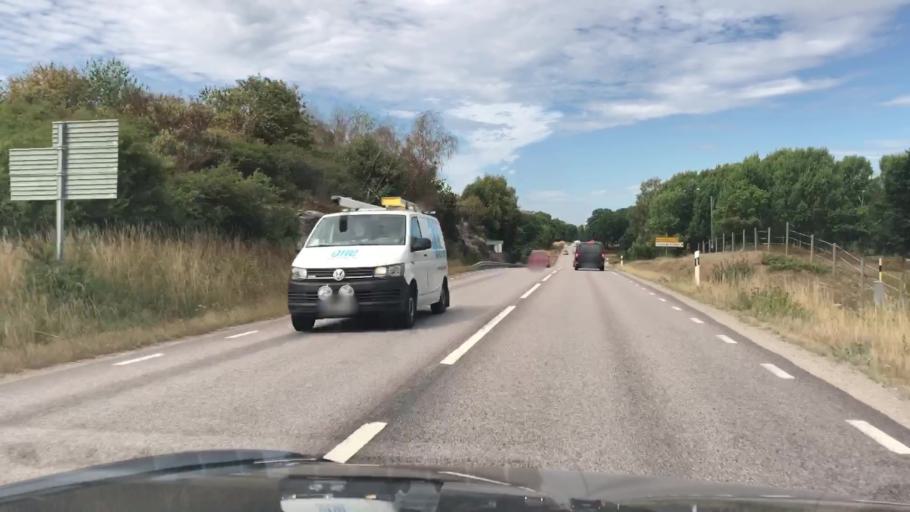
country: SE
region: Blekinge
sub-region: Karlskrona Kommun
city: Sturko
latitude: 56.1889
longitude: 15.7097
